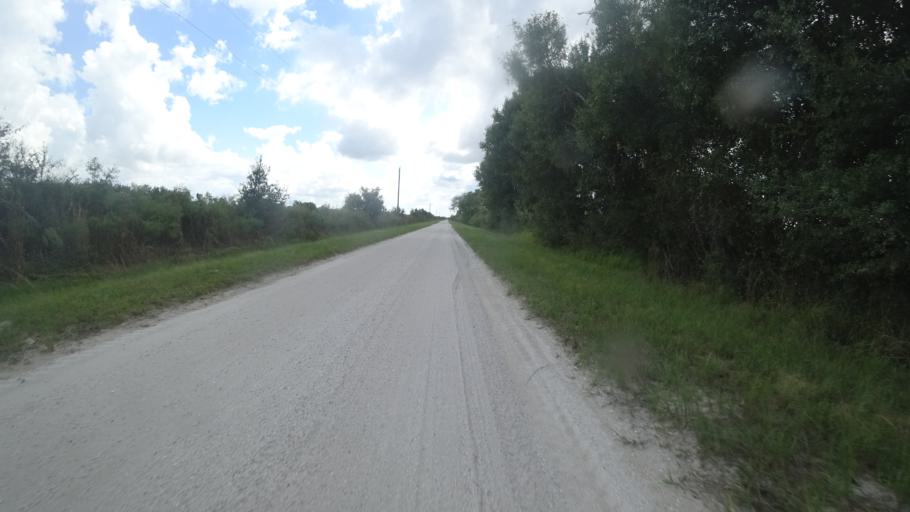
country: US
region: Florida
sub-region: Hillsborough County
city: Wimauma
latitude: 27.5714
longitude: -82.1741
